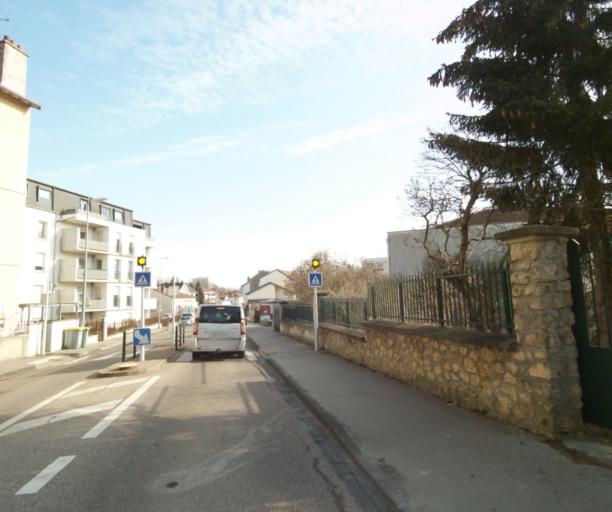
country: FR
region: Lorraine
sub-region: Departement de Meurthe-et-Moselle
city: Laxou
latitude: 48.6828
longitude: 6.1490
